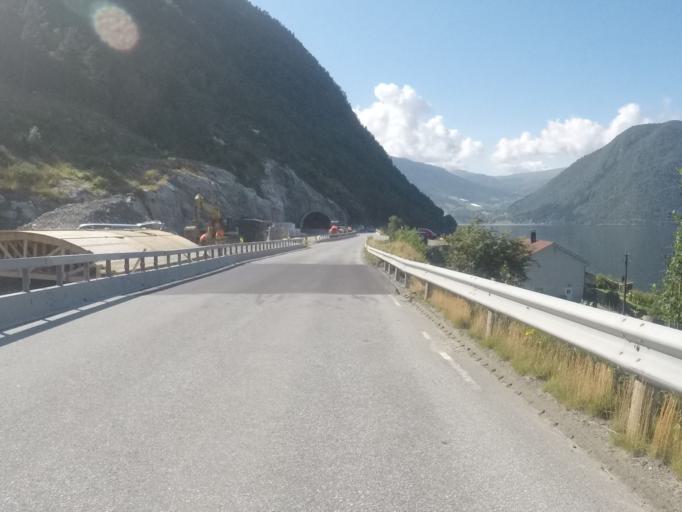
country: NO
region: Sogn og Fjordane
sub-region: Vik
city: Vikoyri
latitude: 61.1190
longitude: 6.6023
